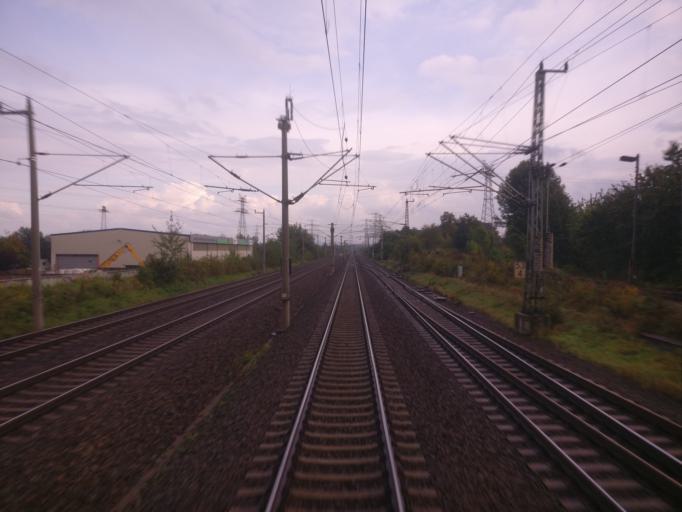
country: DE
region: Saxony
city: Heidenau
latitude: 50.9943
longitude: 13.8372
